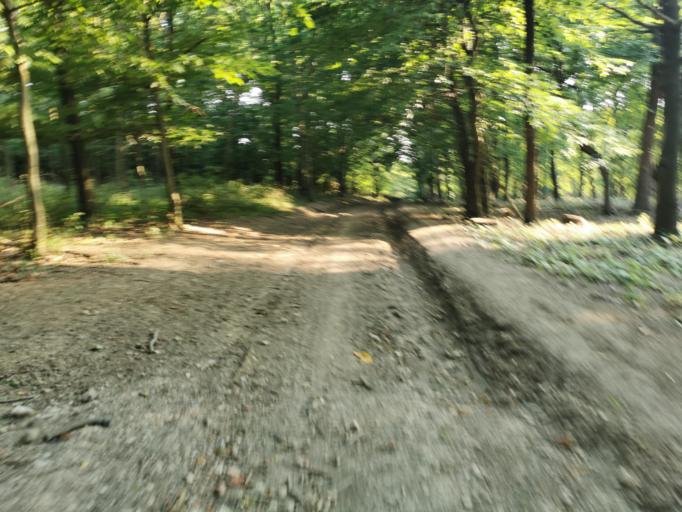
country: CZ
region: South Moravian
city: Sudomerice
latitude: 48.8140
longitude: 17.2970
